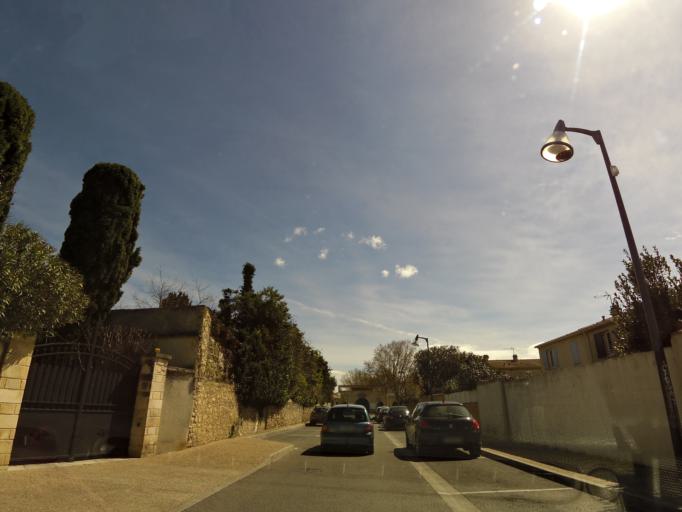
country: FR
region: Languedoc-Roussillon
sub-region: Departement du Gard
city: Milhaud
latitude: 43.7880
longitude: 4.3089
